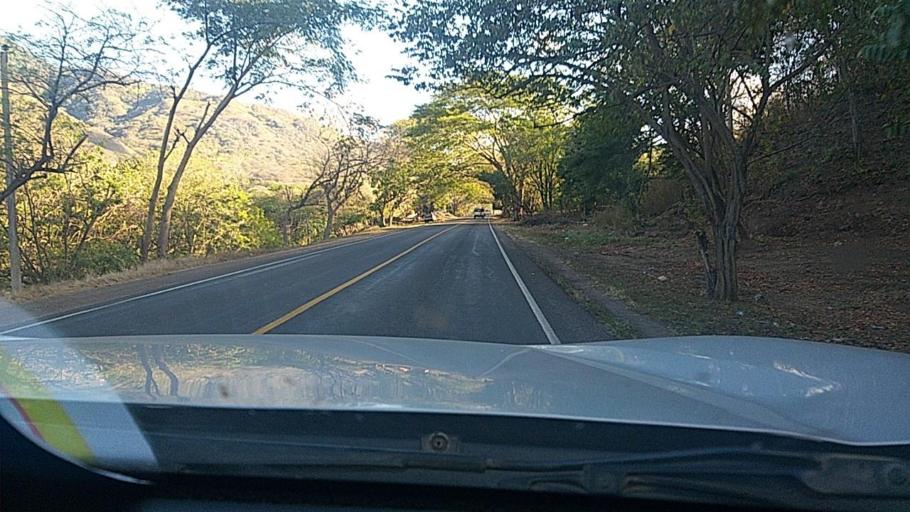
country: NI
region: Esteli
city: Condega
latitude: 13.2912
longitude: -86.3471
